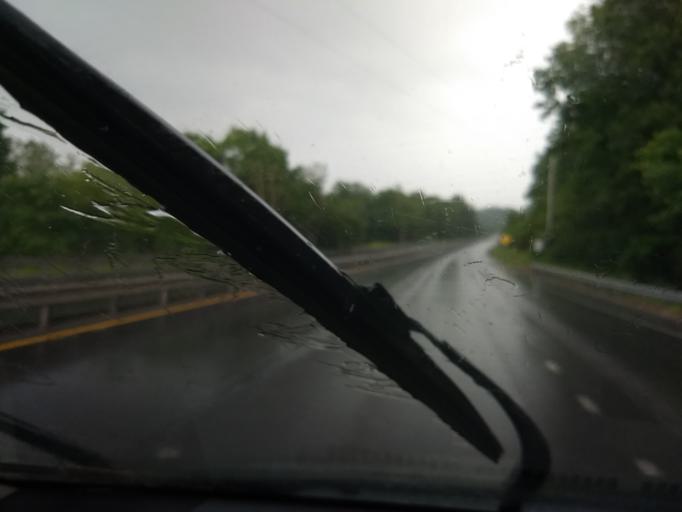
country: US
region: Pennsylvania
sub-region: Armstrong County
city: Apollo
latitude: 40.5267
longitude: -79.5943
